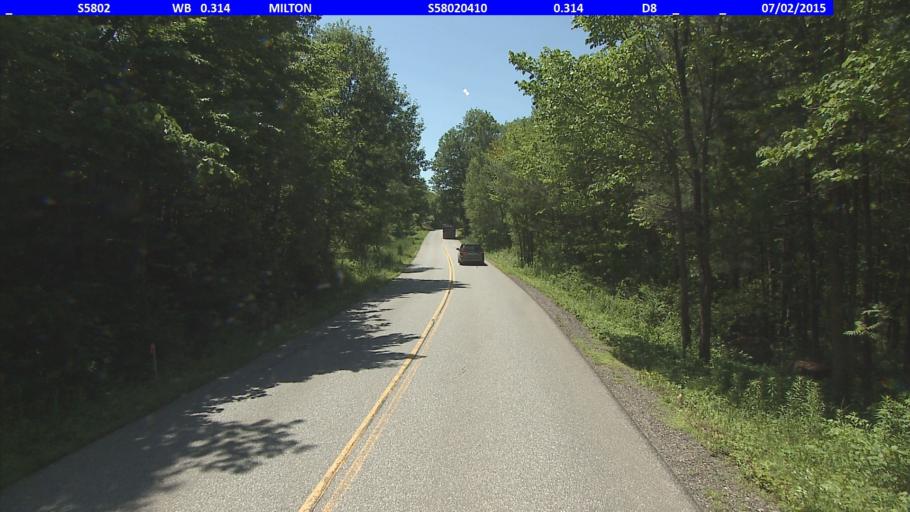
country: US
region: Vermont
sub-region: Chittenden County
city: Colchester
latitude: 44.6130
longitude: -73.2051
